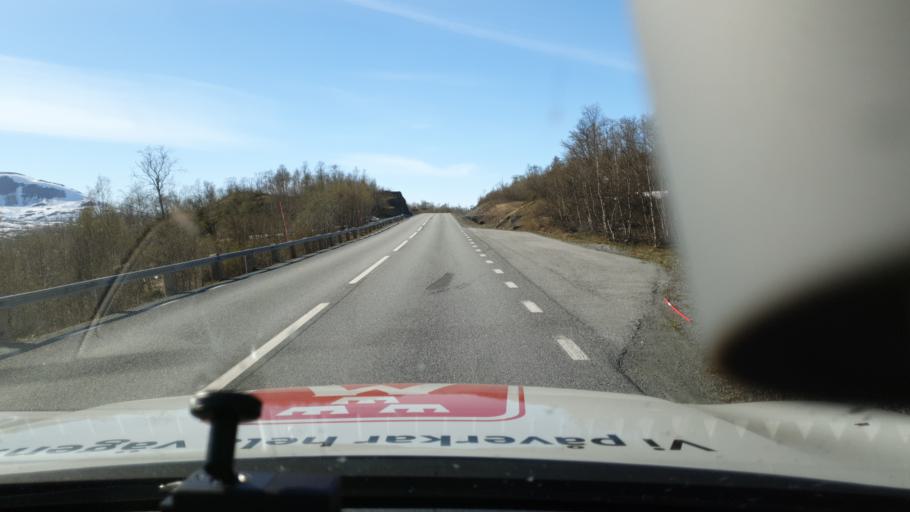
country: NO
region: Nordland
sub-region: Rana
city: Mo i Rana
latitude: 66.0548
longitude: 14.8795
